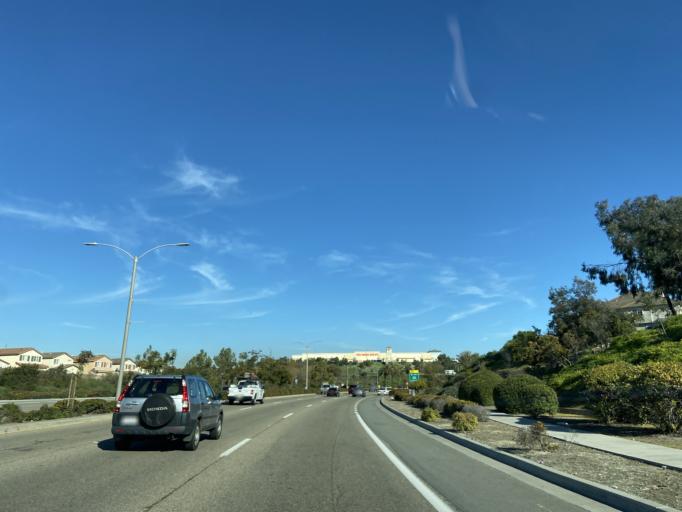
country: US
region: California
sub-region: San Diego County
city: Bonita
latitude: 32.6319
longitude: -116.9754
